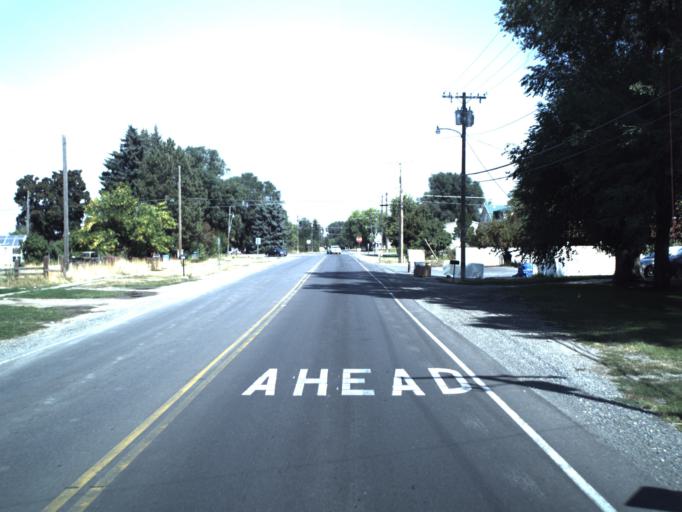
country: US
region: Utah
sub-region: Cache County
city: Hyrum
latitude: 41.6390
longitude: -111.8661
